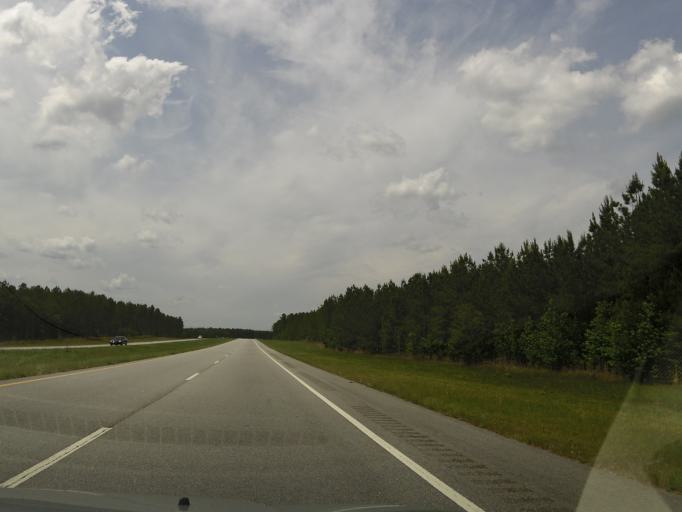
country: US
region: Georgia
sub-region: Jefferson County
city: Wadley
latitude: 32.7811
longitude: -82.3899
